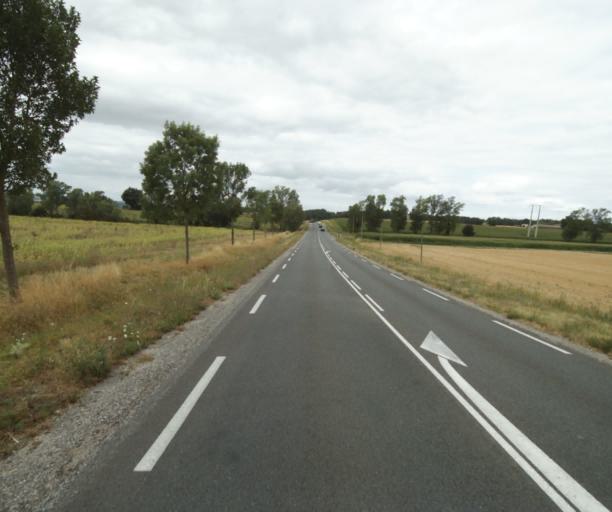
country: FR
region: Midi-Pyrenees
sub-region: Departement de la Haute-Garonne
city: Revel
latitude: 43.4886
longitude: 2.0350
